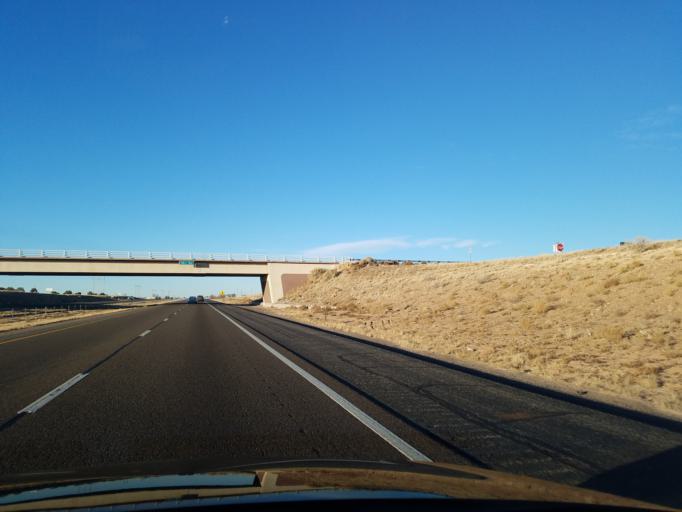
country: US
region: New Mexico
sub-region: Sandoval County
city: Santo Domingo Pueblo
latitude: 35.4710
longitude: -106.3031
